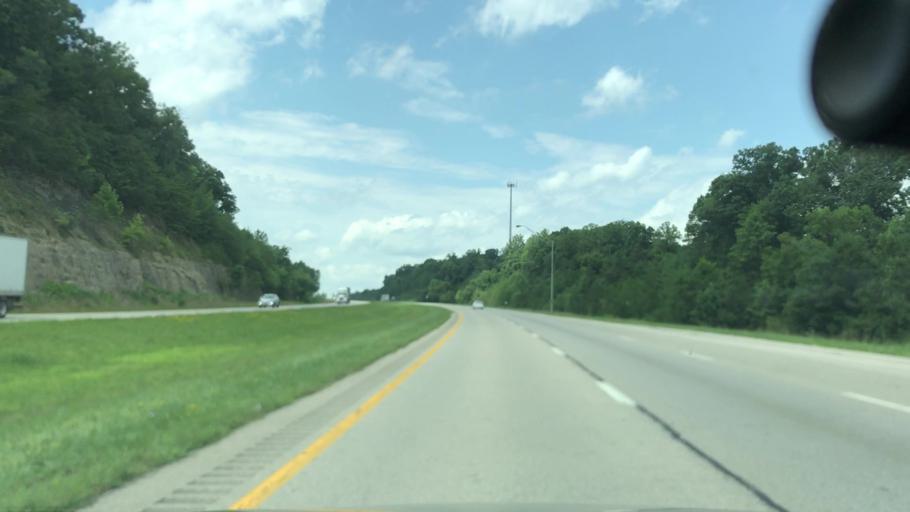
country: US
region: Ohio
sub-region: Jackson County
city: Jackson
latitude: 39.0763
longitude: -82.6308
